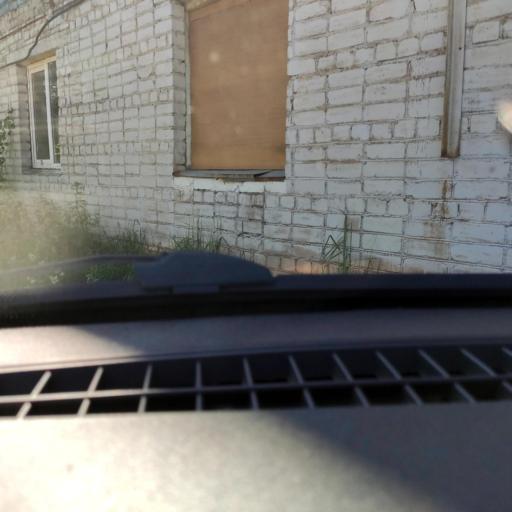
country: RU
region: Bashkortostan
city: Ufa
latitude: 54.8449
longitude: 56.1137
